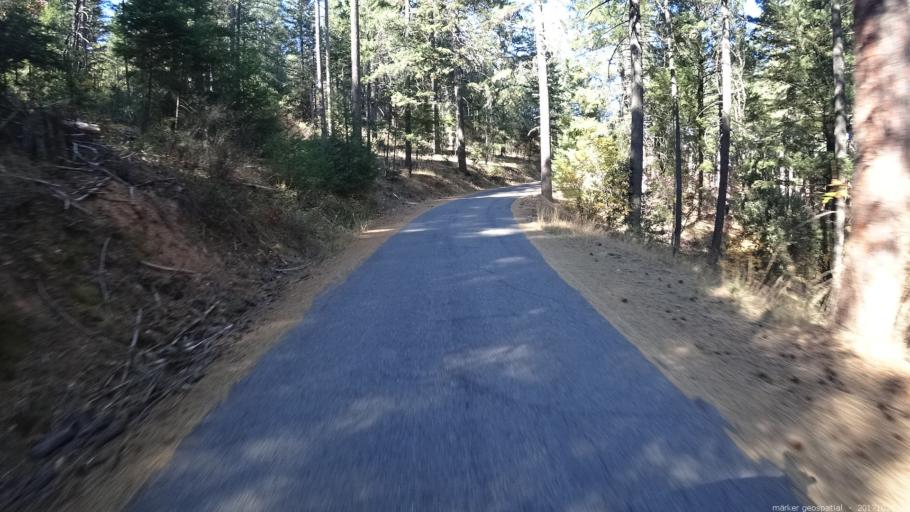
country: US
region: California
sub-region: Trinity County
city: Lewiston
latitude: 40.8148
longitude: -122.6380
